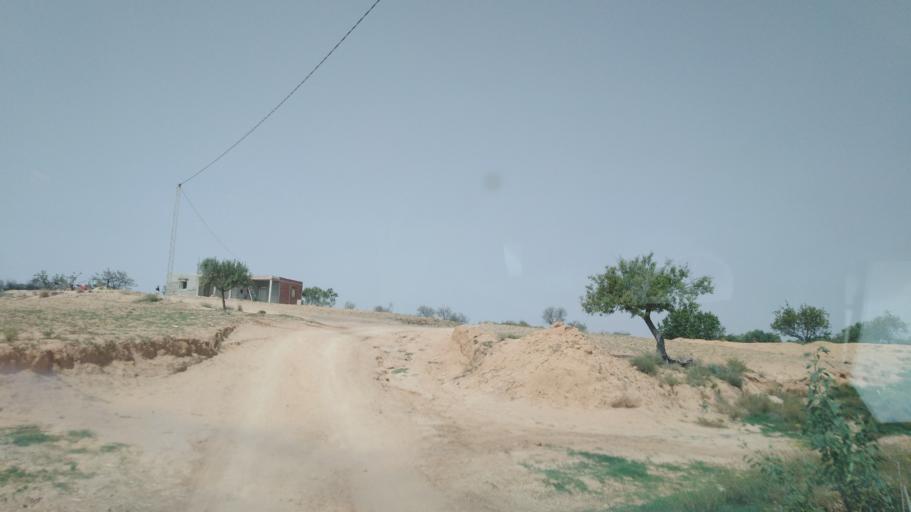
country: TN
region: Safaqis
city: Sfax
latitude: 34.6388
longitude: 10.5678
